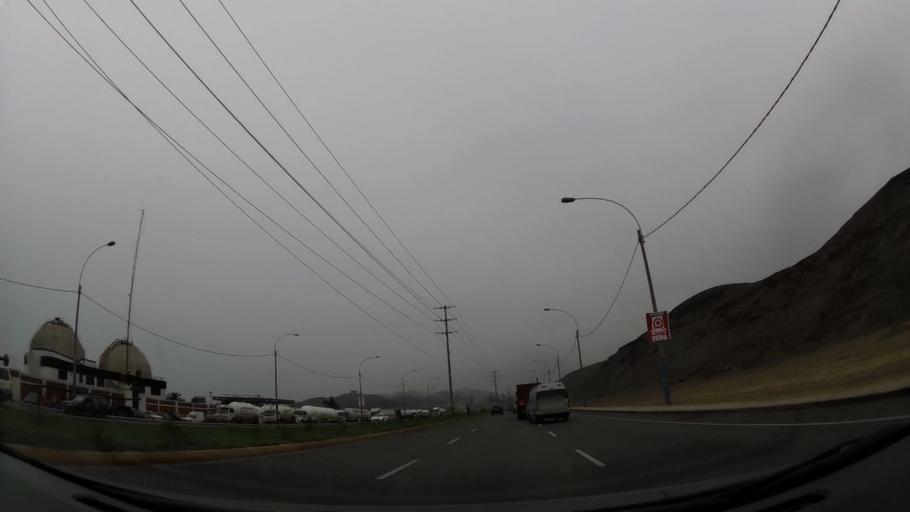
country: PE
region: Lima
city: Ventanilla
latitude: -11.9349
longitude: -77.1306
